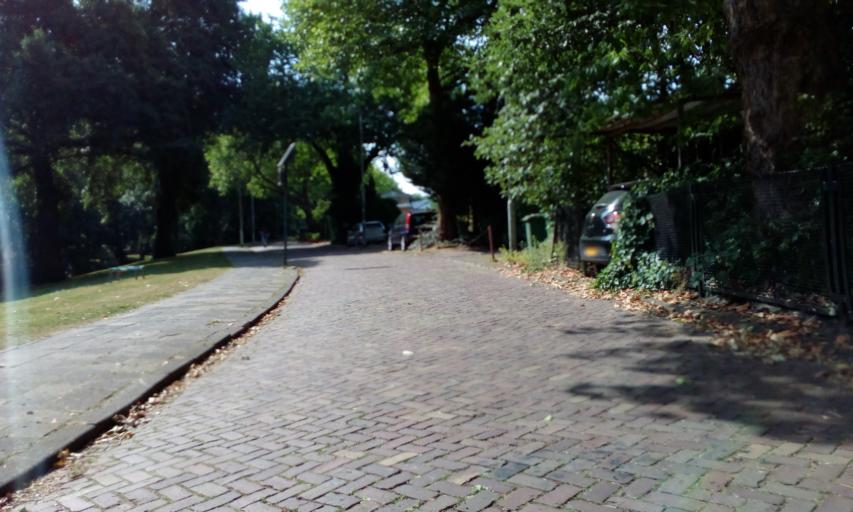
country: NL
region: South Holland
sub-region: Gemeente Rotterdam
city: Rotterdam
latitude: 51.9386
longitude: 4.4862
